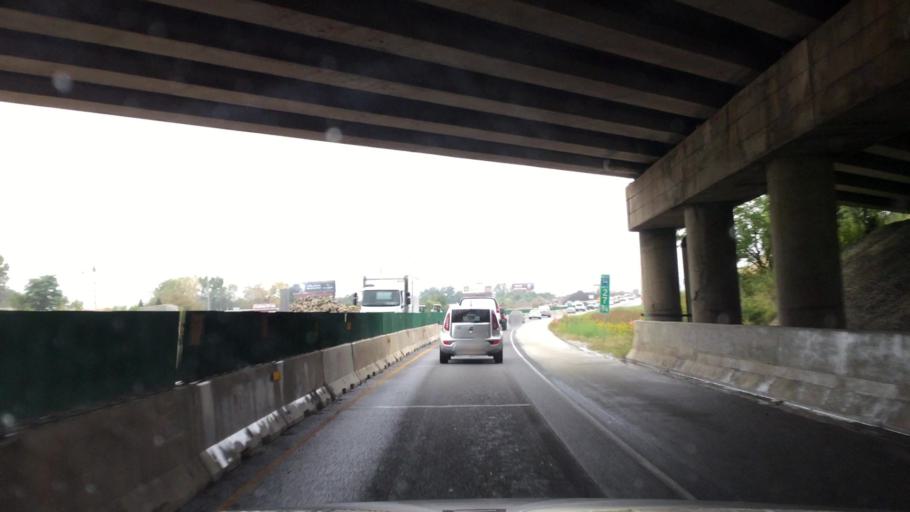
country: US
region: Illinois
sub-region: Cook County
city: Northbrook
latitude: 42.1448
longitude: -87.8301
